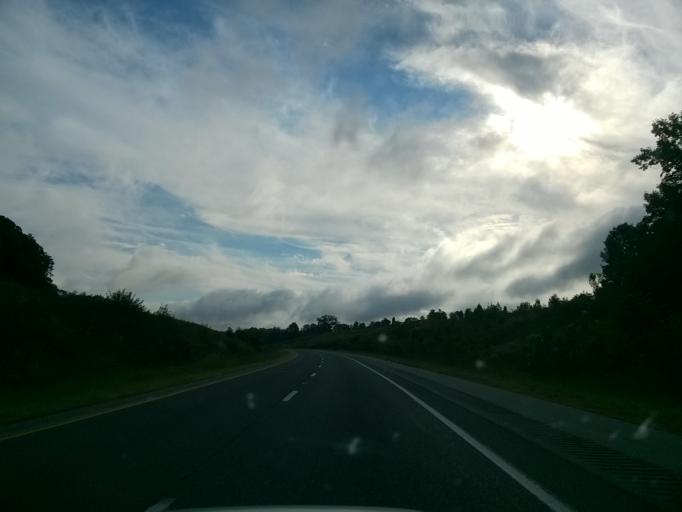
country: US
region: Indiana
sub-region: Dubois County
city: Ferdinand
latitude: 38.2171
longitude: -86.7271
